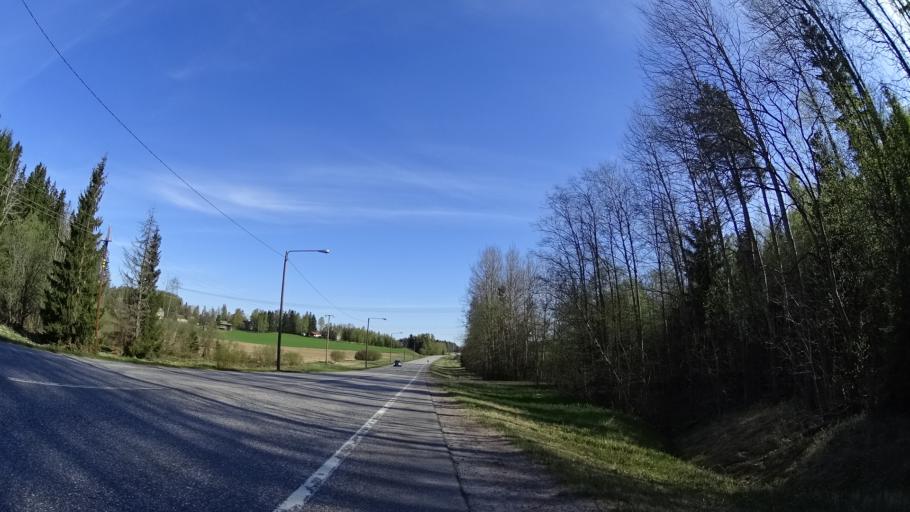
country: FI
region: Uusimaa
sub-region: Helsinki
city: Nurmijaervi
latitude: 60.3890
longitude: 24.8089
